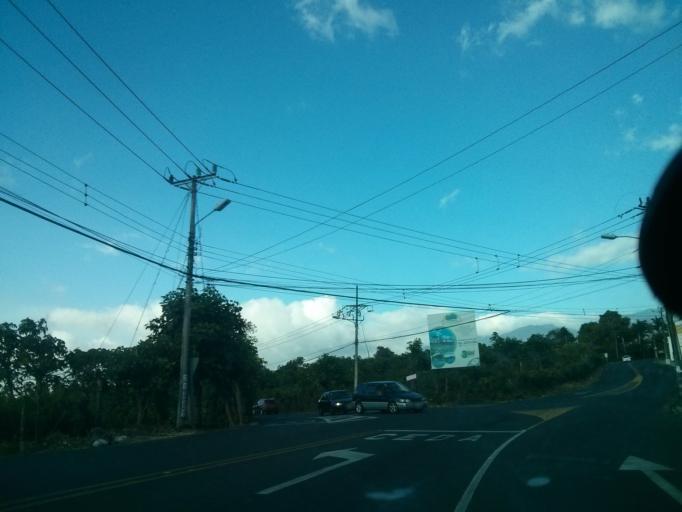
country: CR
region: San Jose
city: Granadilla
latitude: 9.9262
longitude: -84.0274
